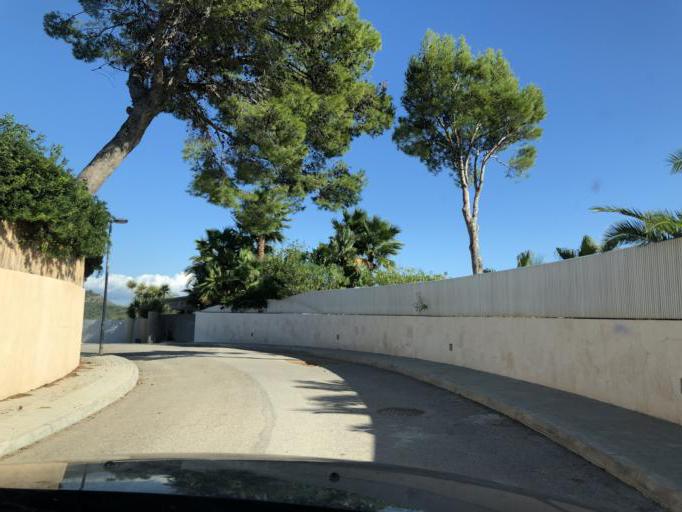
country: ES
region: Balearic Islands
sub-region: Illes Balears
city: Camp de Mar
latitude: 39.5380
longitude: 2.4077
